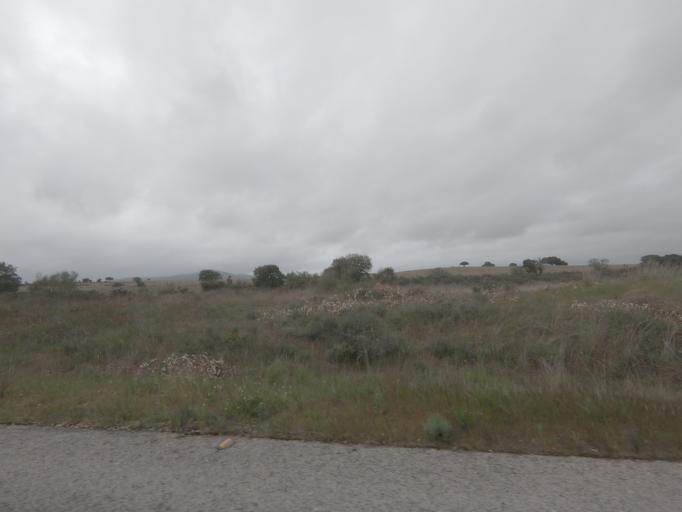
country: ES
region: Extremadura
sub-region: Provincia de Caceres
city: Malpartida de Caceres
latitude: 39.3269
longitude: -6.4937
